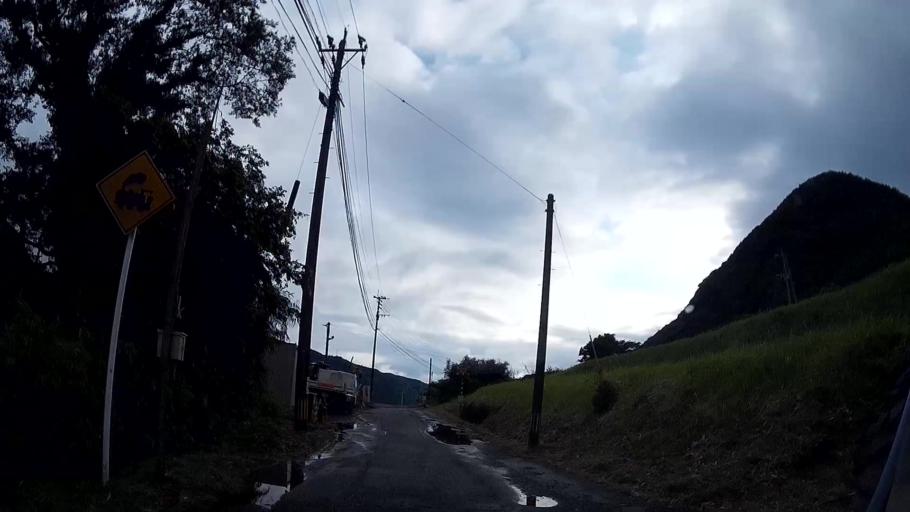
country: JP
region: Kumamoto
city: Ozu
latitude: 32.8795
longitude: 130.9604
